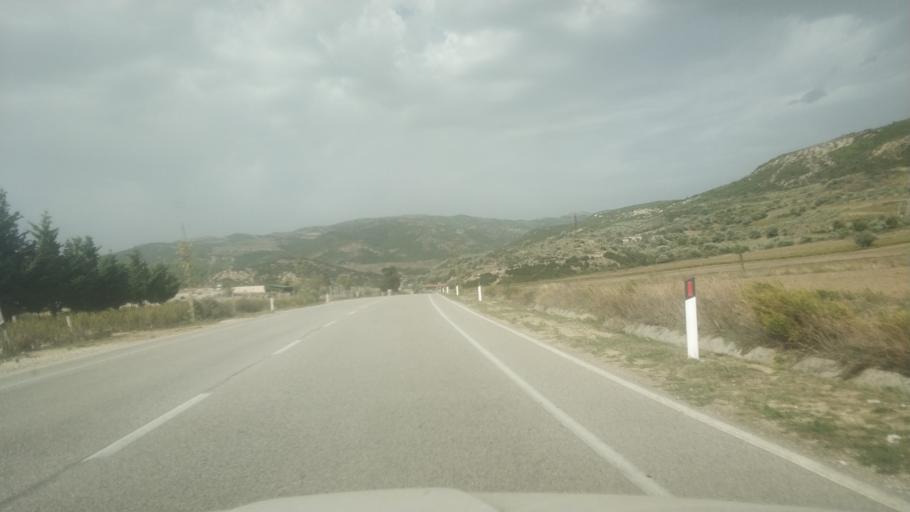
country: AL
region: Gjirokaster
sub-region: Rrethi i Tepelenes
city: Memaliaj
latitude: 40.3703
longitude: 19.9078
